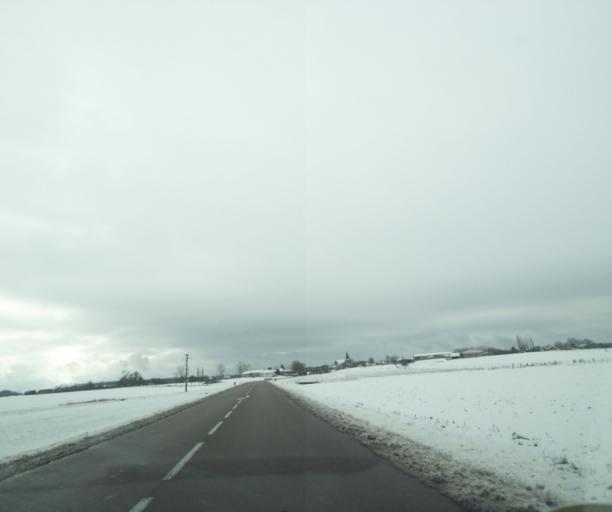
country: FR
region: Champagne-Ardenne
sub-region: Departement de la Haute-Marne
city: Montier-en-Der
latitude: 48.4395
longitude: 4.7286
